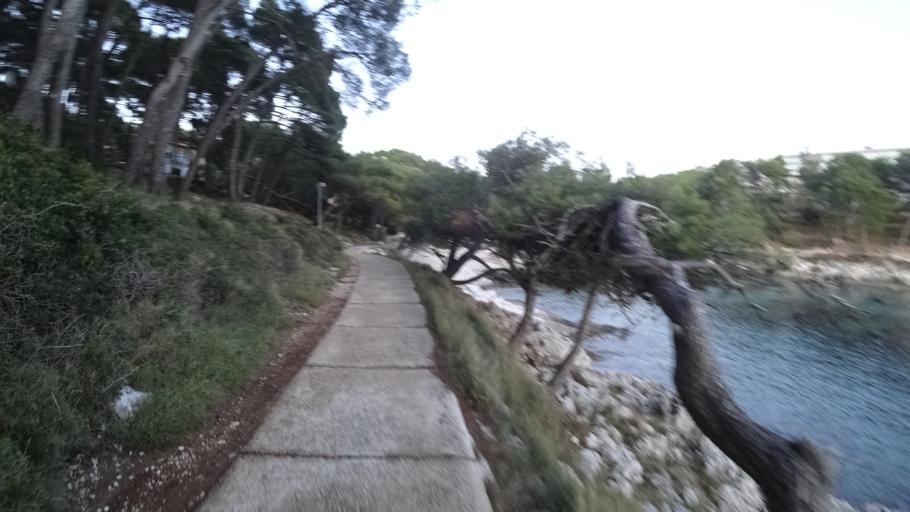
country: HR
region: Primorsko-Goranska
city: Mali Losinj
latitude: 44.5241
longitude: 14.4574
